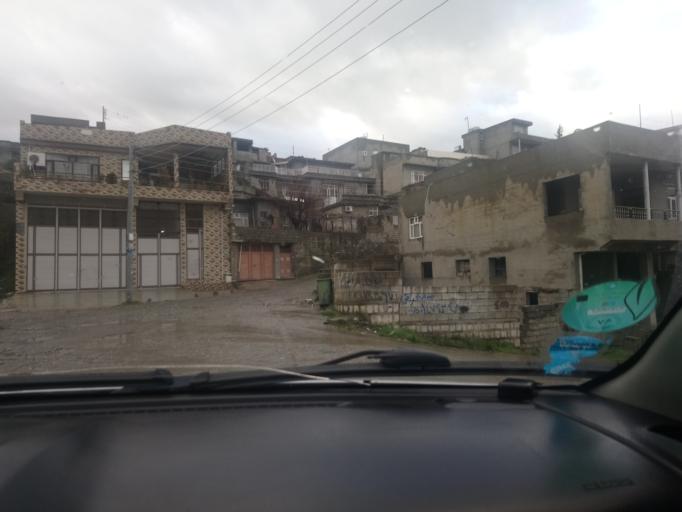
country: IQ
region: As Sulaymaniyah
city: Qeladize
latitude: 36.1813
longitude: 45.1229
